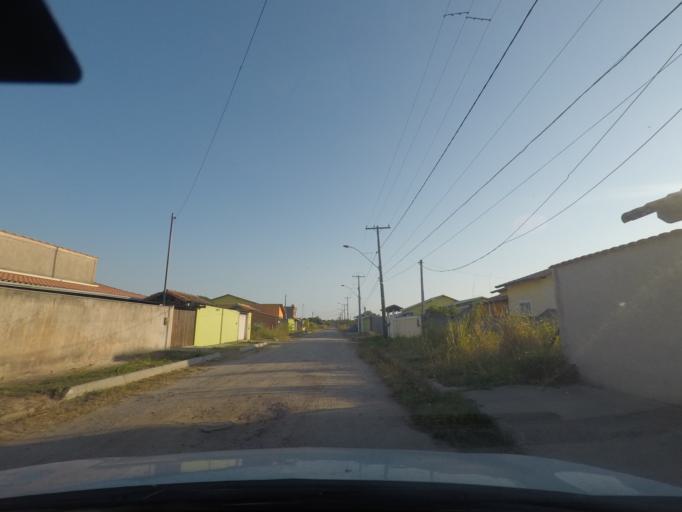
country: BR
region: Rio de Janeiro
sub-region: Marica
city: Marica
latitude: -22.9622
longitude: -42.9280
